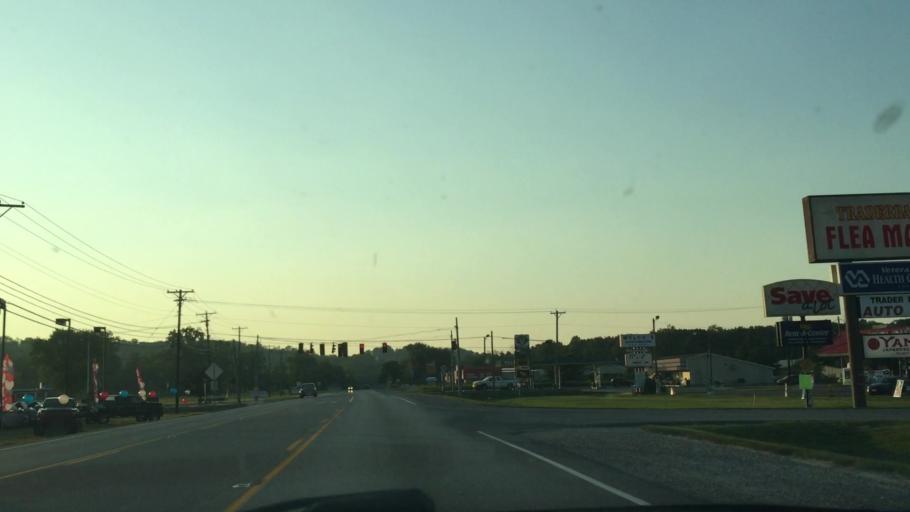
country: US
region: Kentucky
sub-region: Carroll County
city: Carrollton
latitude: 38.6633
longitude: -85.1407
